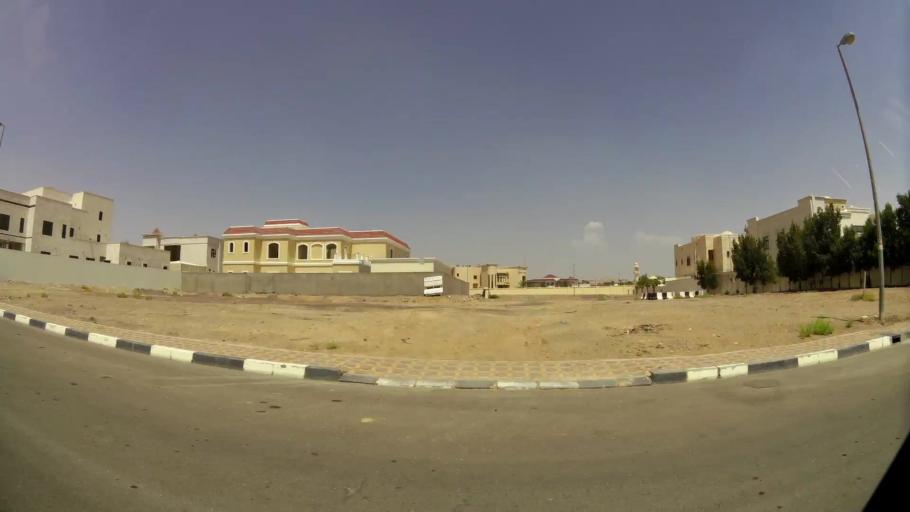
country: AE
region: Abu Dhabi
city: Al Ain
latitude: 24.2533
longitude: 55.6986
